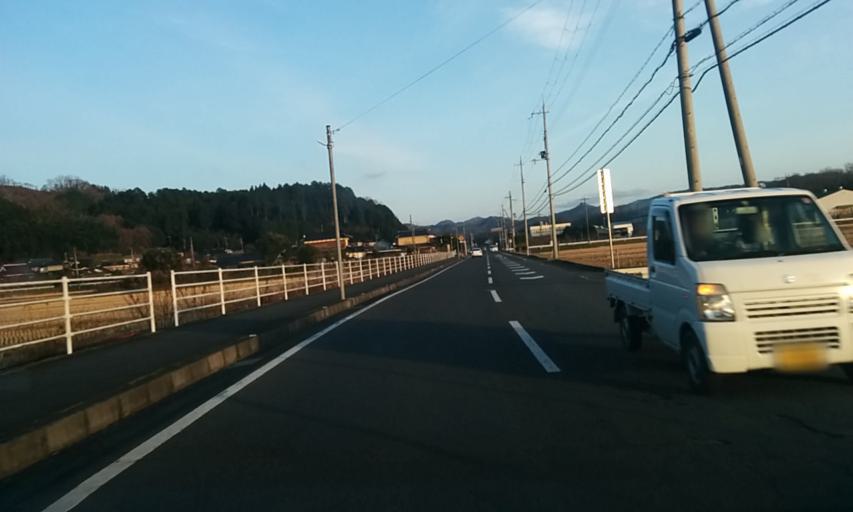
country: JP
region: Kyoto
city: Ayabe
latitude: 35.3136
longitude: 135.2329
